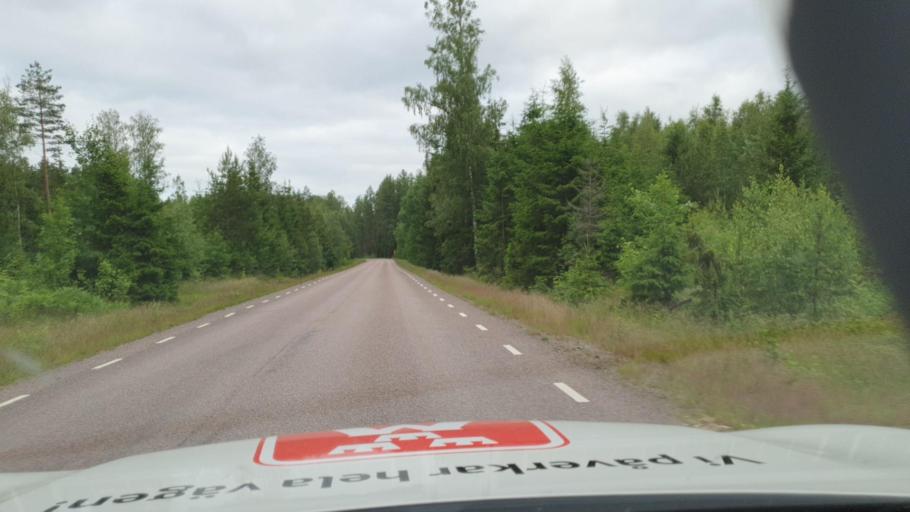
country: SE
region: Vaermland
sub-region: Forshaga Kommun
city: Forshaga
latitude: 59.4862
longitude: 13.4088
